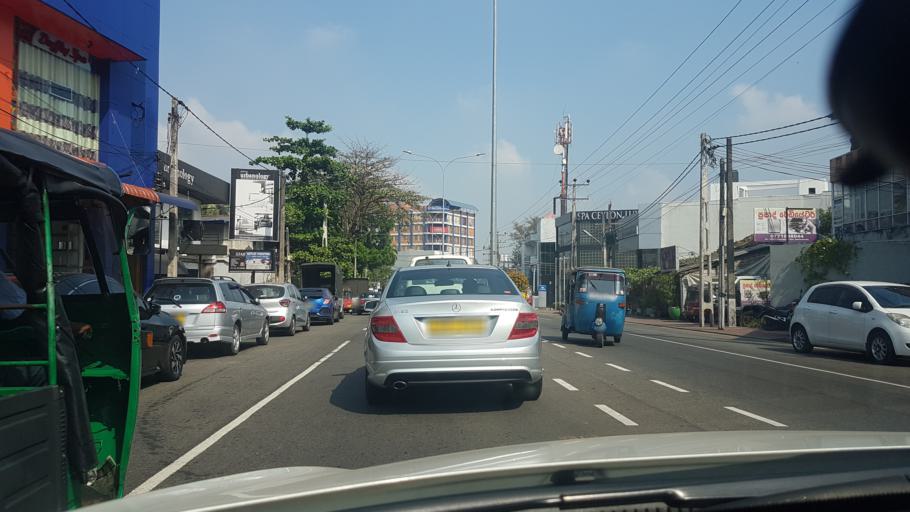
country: LK
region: Western
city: Battaramulla South
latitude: 6.8961
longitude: 79.9229
